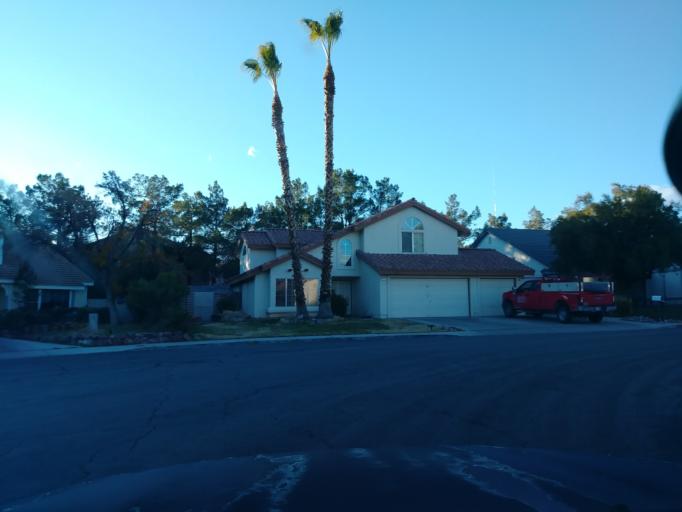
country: US
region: Nevada
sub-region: Clark County
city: Spring Valley
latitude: 36.1465
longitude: -115.2380
